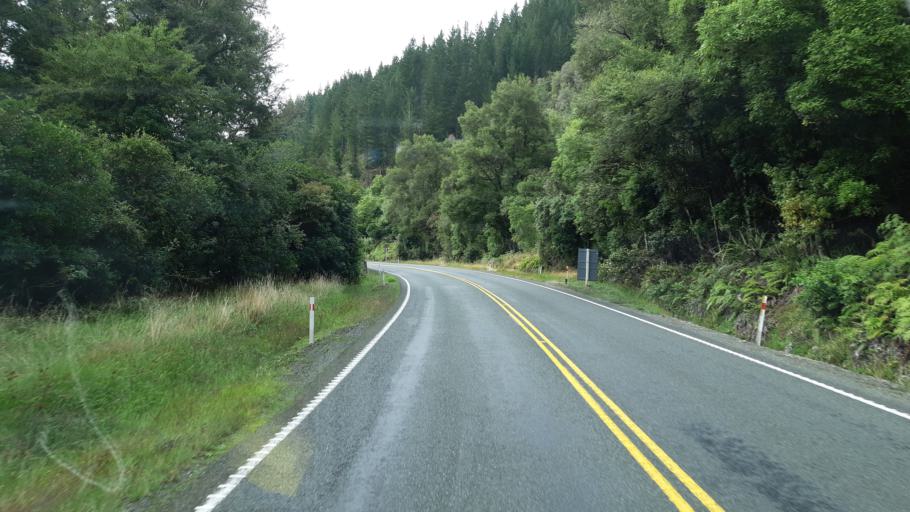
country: NZ
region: West Coast
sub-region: Buller District
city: Westport
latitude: -41.7781
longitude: 172.2469
